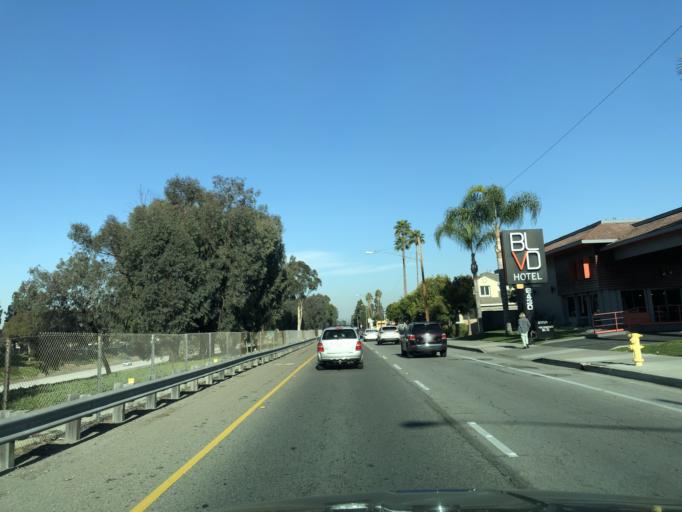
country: US
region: California
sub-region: Orange County
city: Costa Mesa
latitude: 33.6576
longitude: -117.9023
